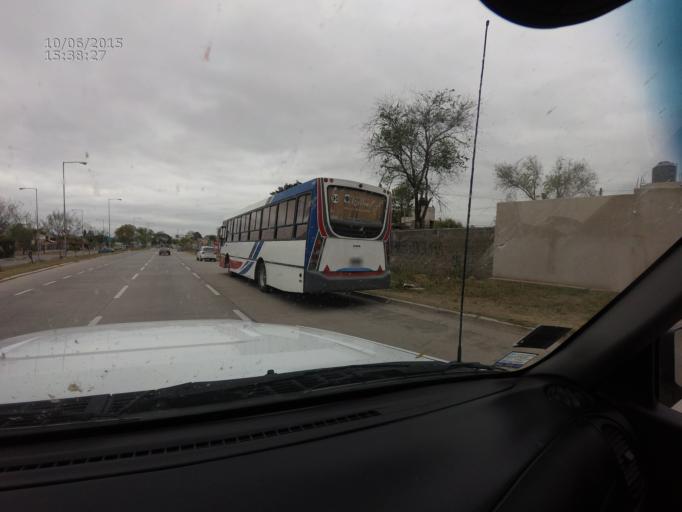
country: AR
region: Cordoba
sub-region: Departamento de Capital
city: Cordoba
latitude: -31.3582
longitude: -64.2261
